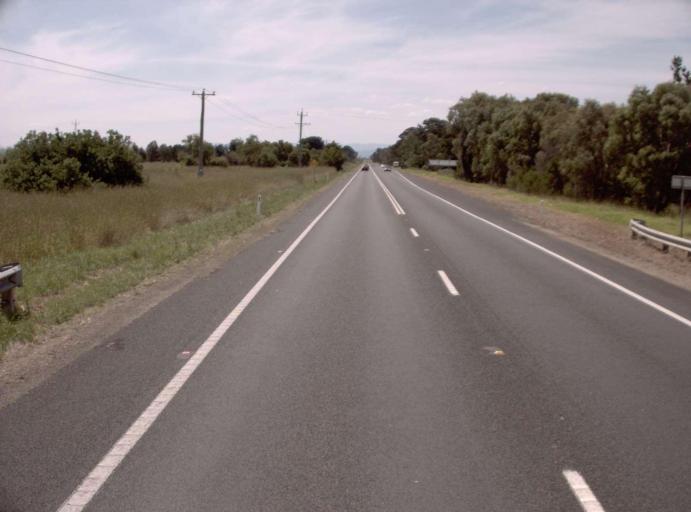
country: AU
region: Victoria
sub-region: Wellington
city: Sale
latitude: -38.0485
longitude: 147.0650
